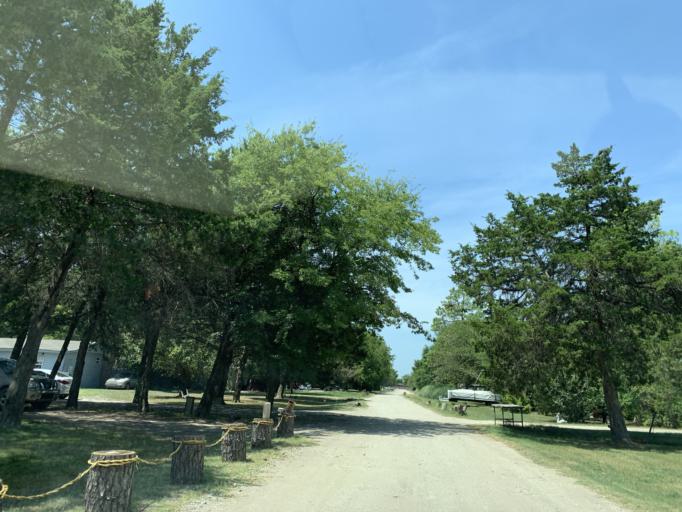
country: US
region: Texas
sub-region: Dallas County
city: Cedar Hill
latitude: 32.6411
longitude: -97.0262
